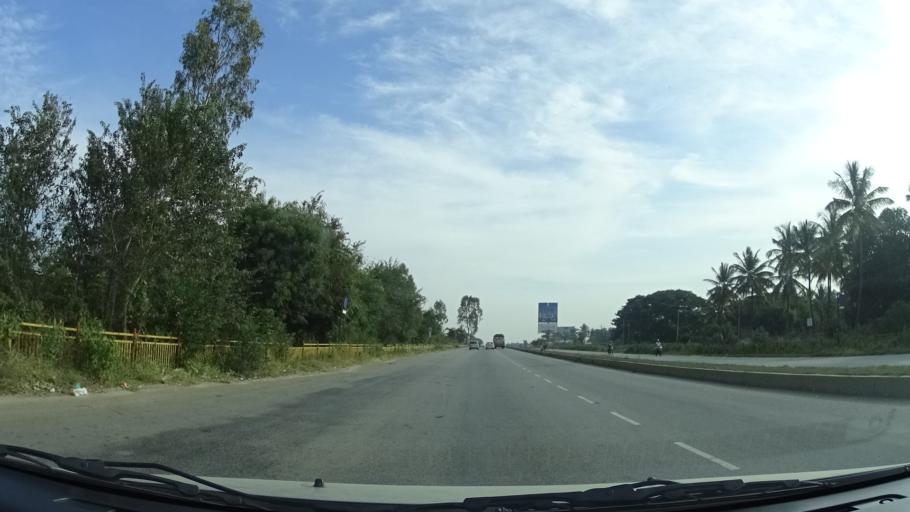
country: IN
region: Karnataka
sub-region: Bangalore Rural
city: Devanhalli
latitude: 13.2244
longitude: 77.6852
